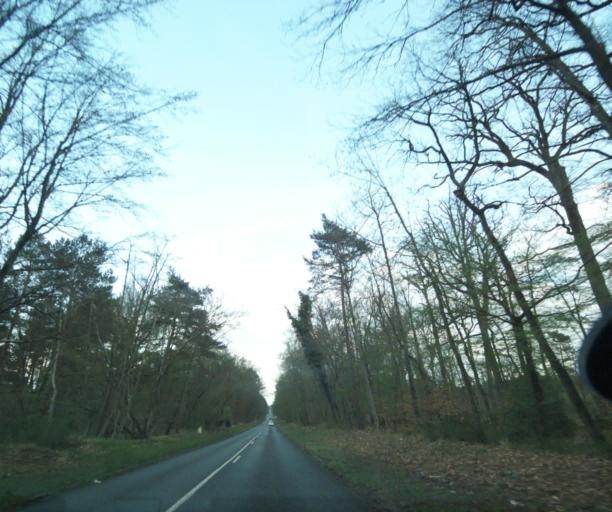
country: FR
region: Ile-de-France
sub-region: Departement de Seine-et-Marne
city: Avon
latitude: 48.3881
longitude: 2.7148
